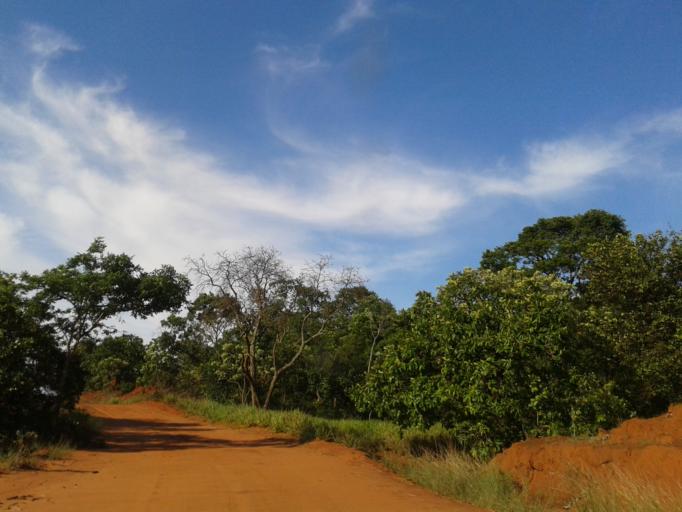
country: BR
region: Minas Gerais
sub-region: Santa Vitoria
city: Santa Vitoria
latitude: -19.1192
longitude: -49.9963
